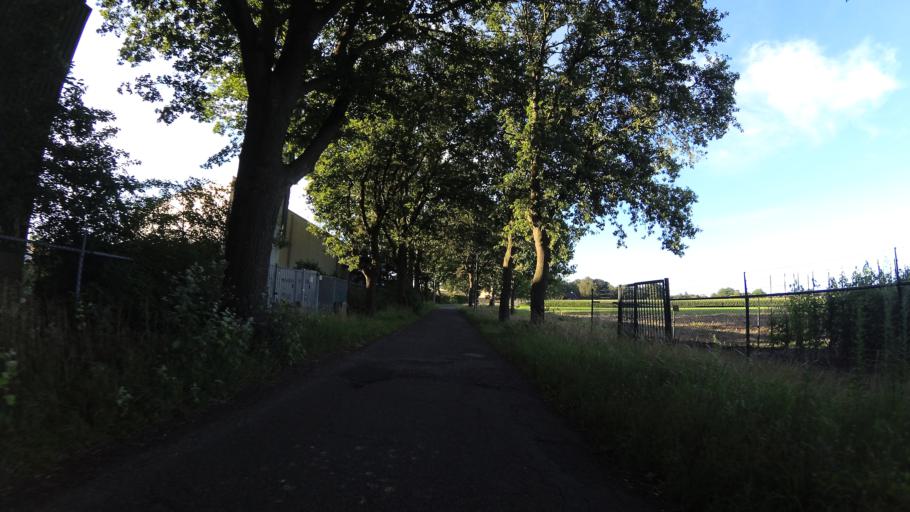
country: NL
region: North Brabant
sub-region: Gemeente Breda
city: Hoge Vucht
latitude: 51.6189
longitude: 4.8263
